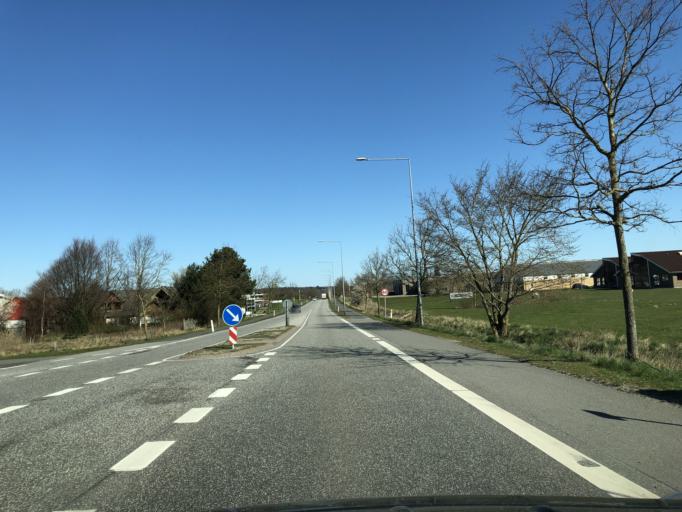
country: DK
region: North Denmark
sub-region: Rebild Kommune
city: Stovring
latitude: 56.8776
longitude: 9.8395
